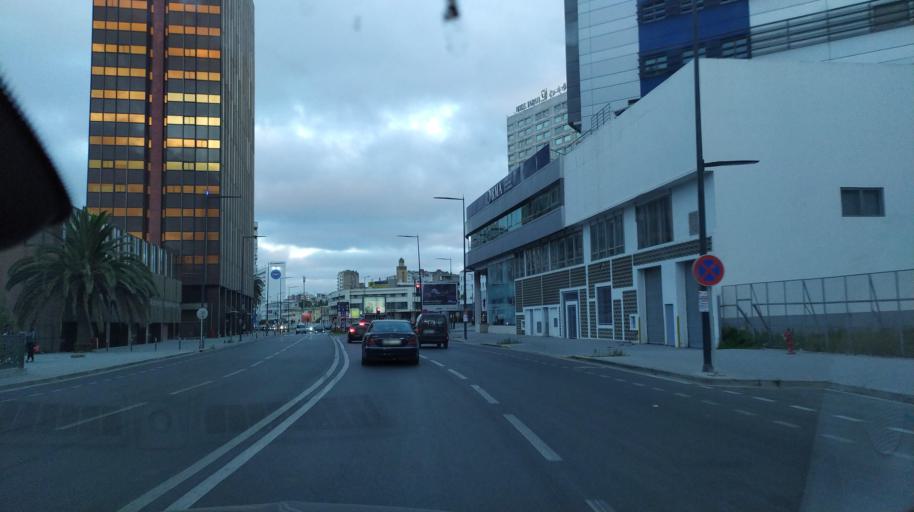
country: MA
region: Grand Casablanca
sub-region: Casablanca
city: Casablanca
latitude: 33.5976
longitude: -7.6116
